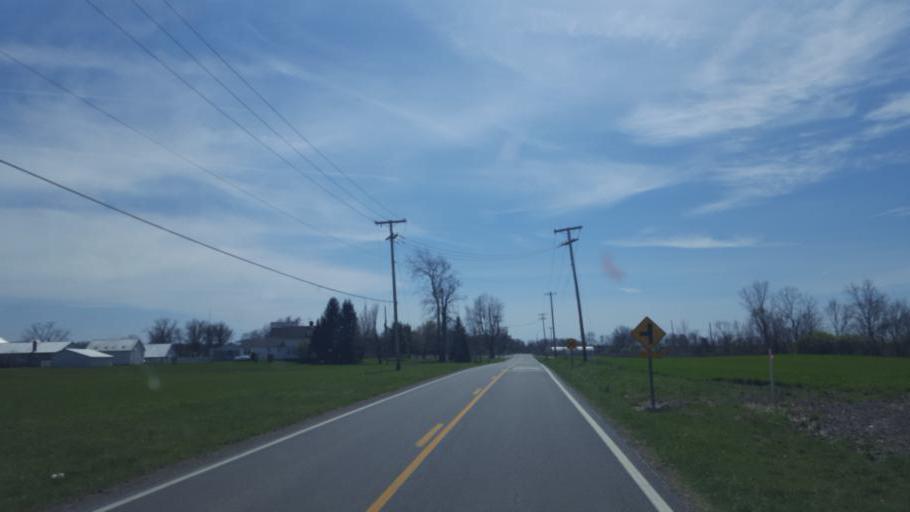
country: US
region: Ohio
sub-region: Delaware County
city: Delaware
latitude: 40.3196
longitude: -83.0486
